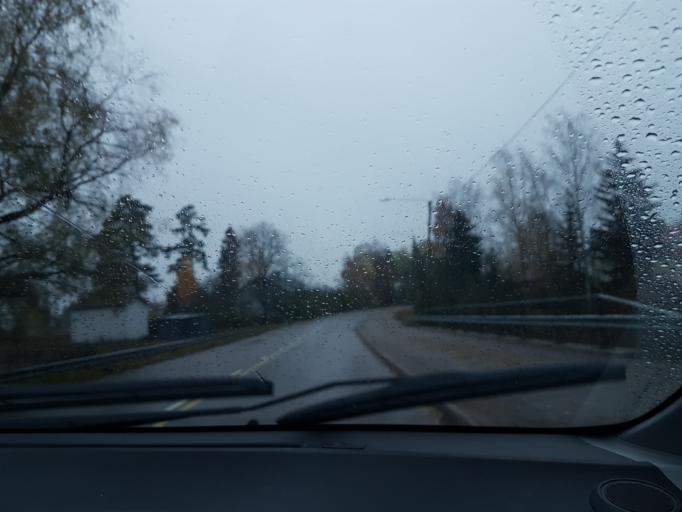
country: FI
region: Uusimaa
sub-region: Helsinki
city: Jaervenpaeae
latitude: 60.5734
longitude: 25.1503
